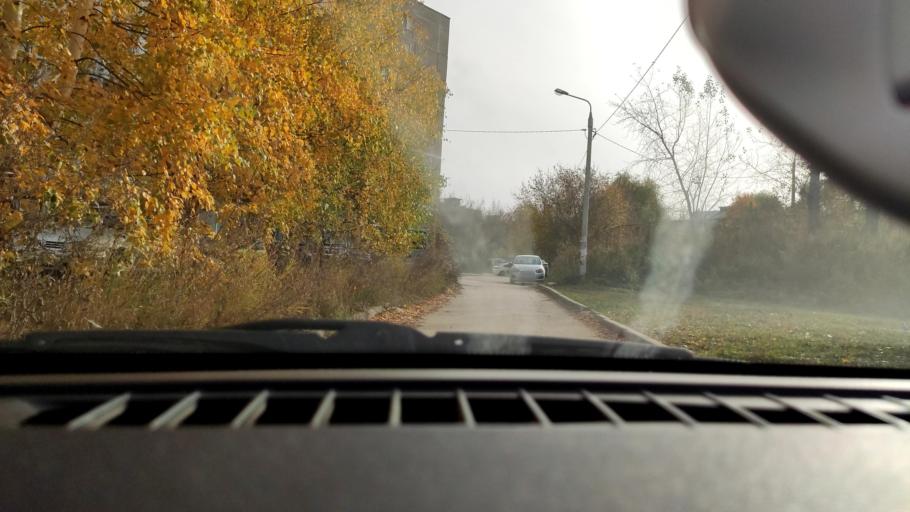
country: RU
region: Perm
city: Perm
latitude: 57.9684
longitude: 56.2136
